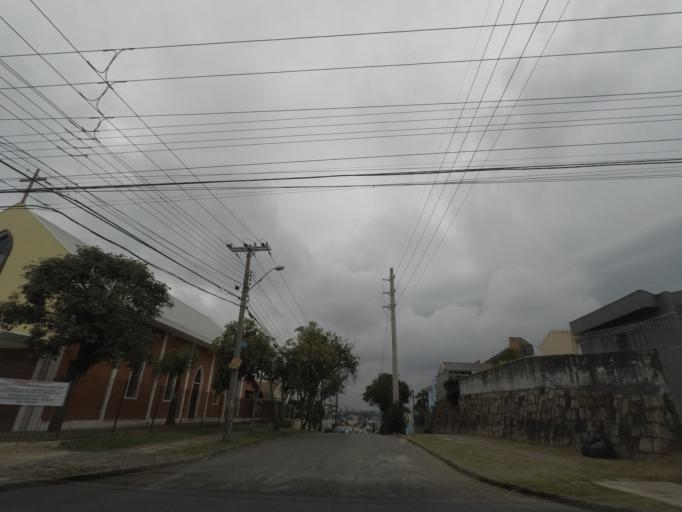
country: BR
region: Parana
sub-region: Curitiba
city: Curitiba
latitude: -25.4647
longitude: -49.2598
